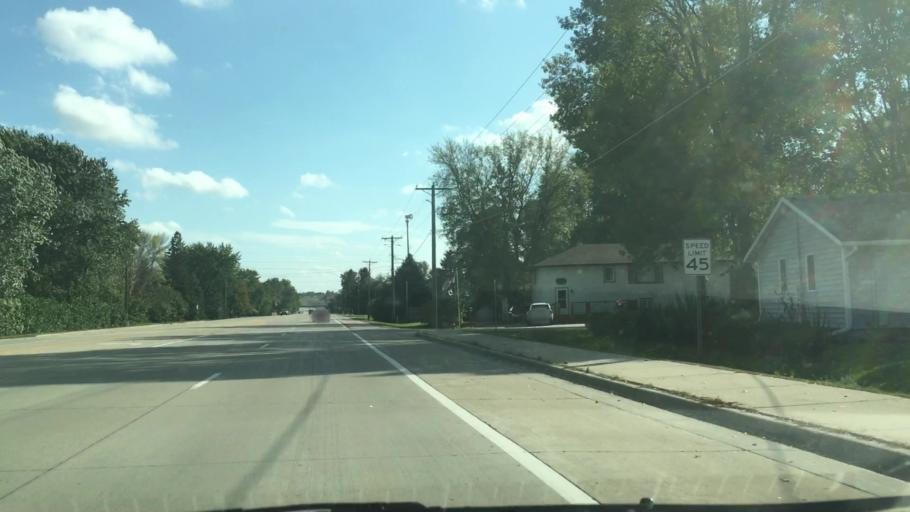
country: US
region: Minnesota
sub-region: Olmsted County
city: Rochester
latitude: 43.9854
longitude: -92.4414
